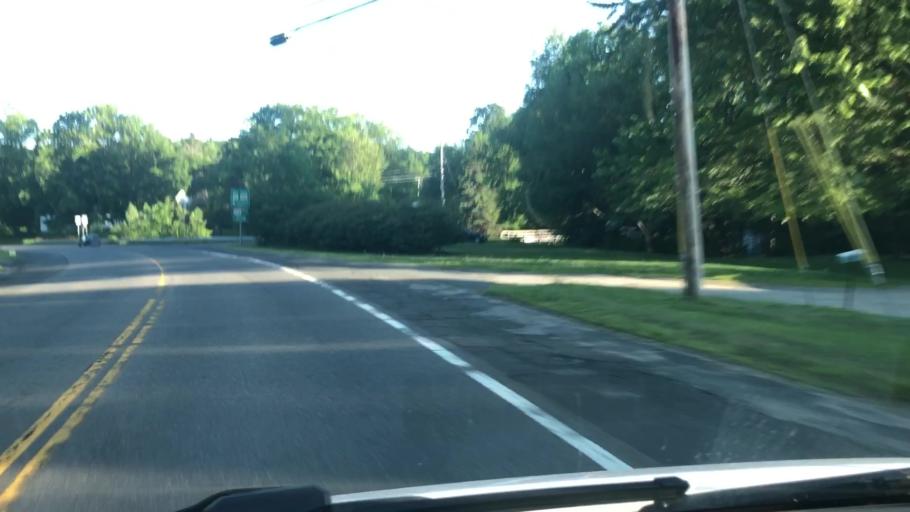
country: US
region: Massachusetts
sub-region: Hampshire County
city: Chesterfield
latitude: 42.4458
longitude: -72.8024
